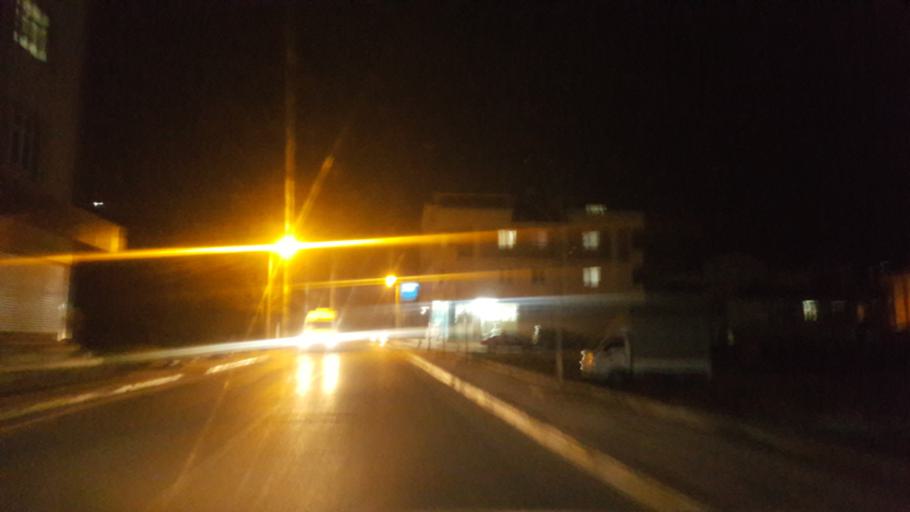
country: TR
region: Kocaeli
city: Darica
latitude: 40.7757
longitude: 29.3865
